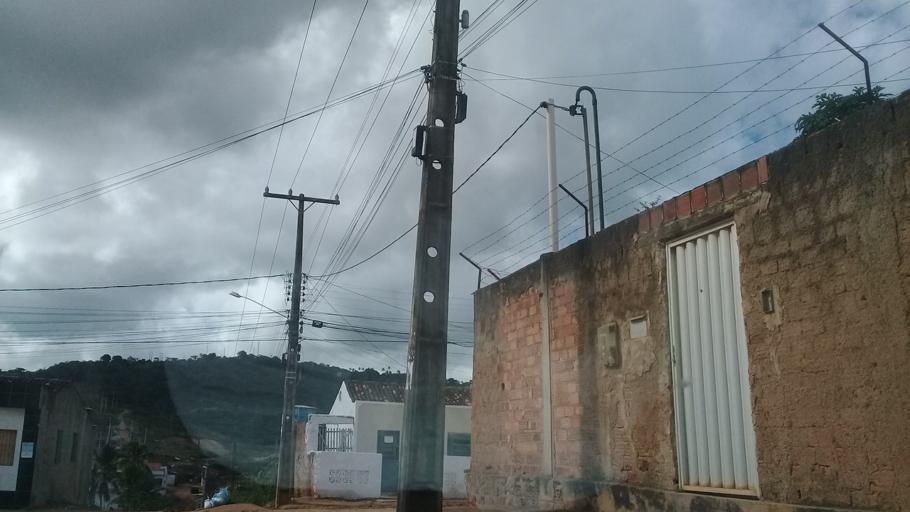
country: BR
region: Pernambuco
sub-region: Vitoria De Santo Antao
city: Vitoria de Santo Antao
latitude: -8.1322
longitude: -35.2944
